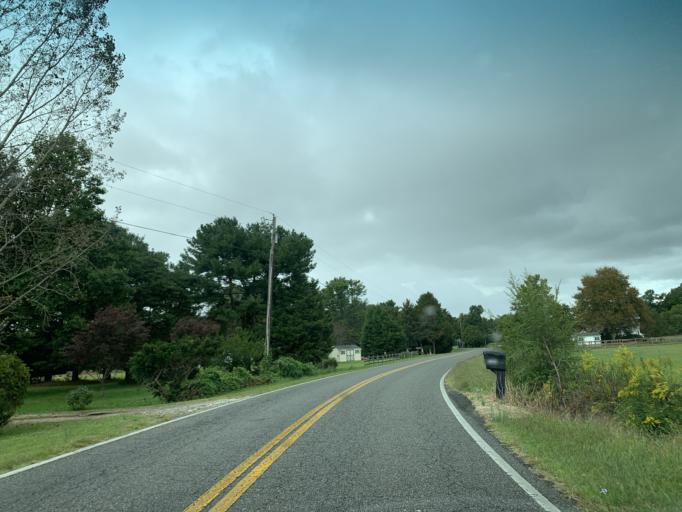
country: US
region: Maryland
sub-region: Caroline County
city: Denton
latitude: 38.9080
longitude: -75.8528
